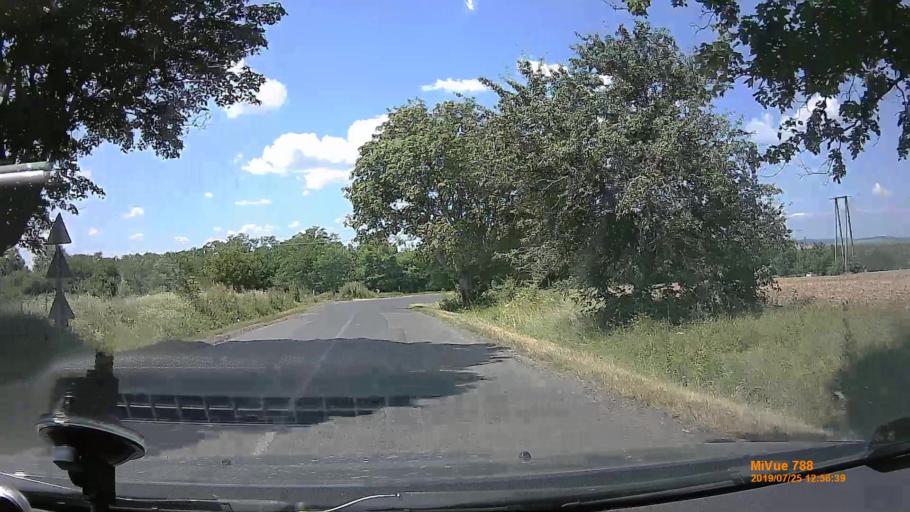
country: HU
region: Borsod-Abauj-Zemplen
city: Encs
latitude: 48.3138
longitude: 21.1670
